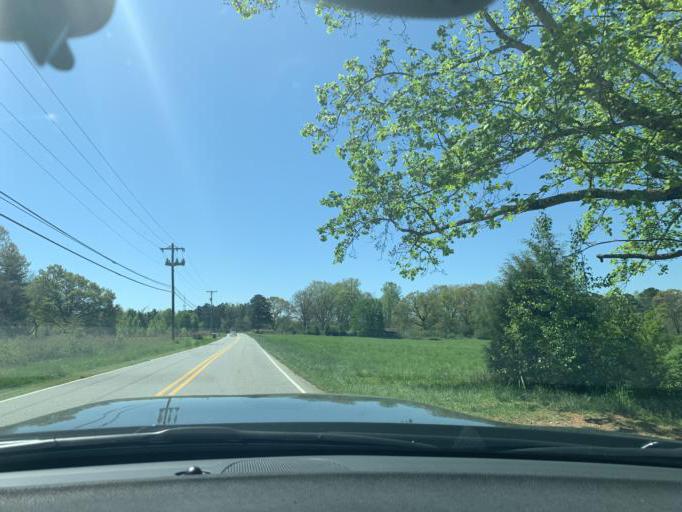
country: US
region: Georgia
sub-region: Forsyth County
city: Cumming
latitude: 34.1740
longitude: -84.1682
